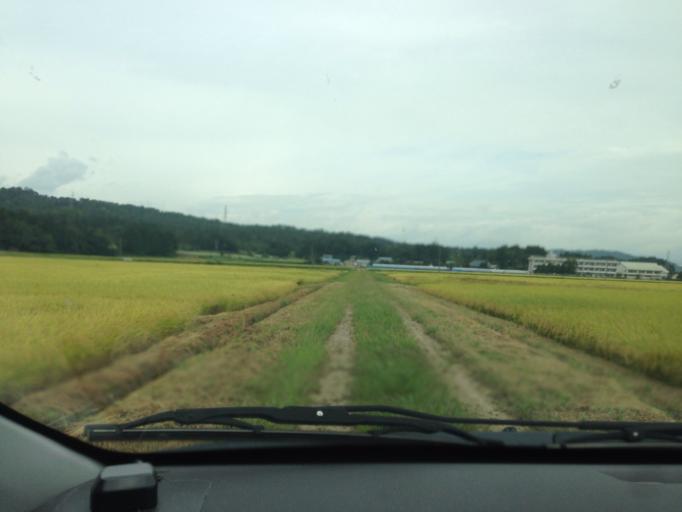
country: JP
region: Fukushima
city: Kitakata
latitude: 37.5836
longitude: 139.8080
